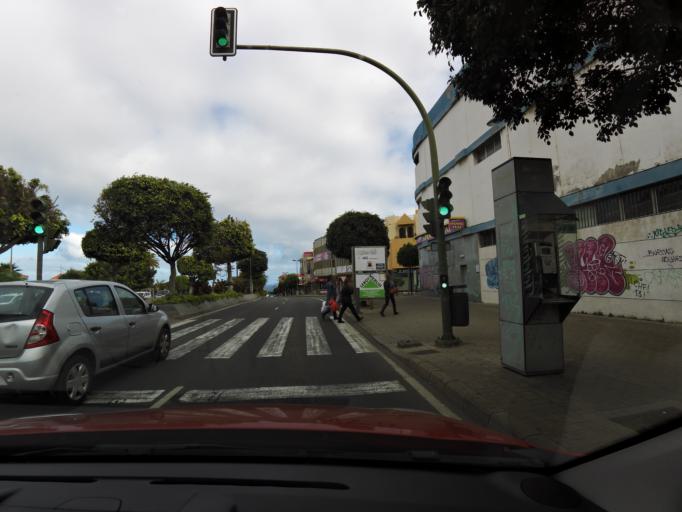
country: ES
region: Canary Islands
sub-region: Provincia de Las Palmas
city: Telde
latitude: 27.9988
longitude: -15.4171
